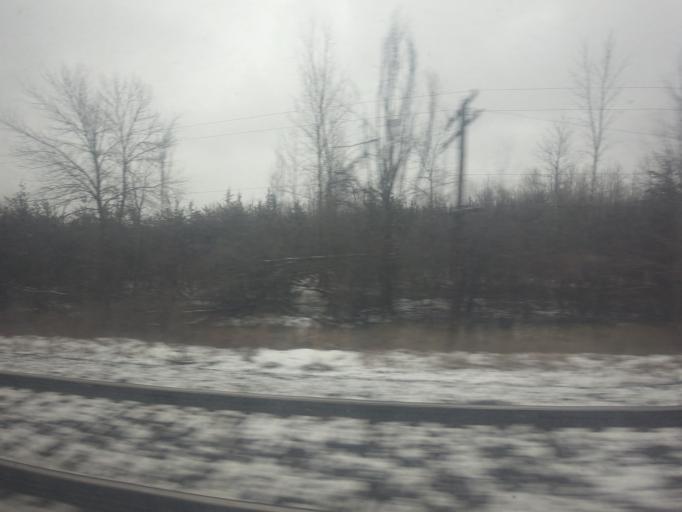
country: CA
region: Ontario
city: Belleville
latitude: 44.1518
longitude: -77.4754
